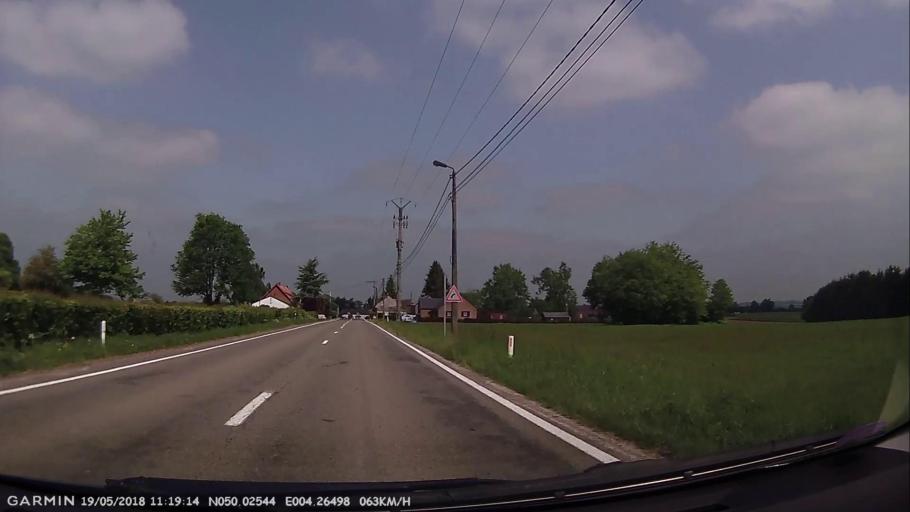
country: BE
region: Wallonia
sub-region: Province du Hainaut
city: Chimay
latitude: 50.0257
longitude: 4.2649
